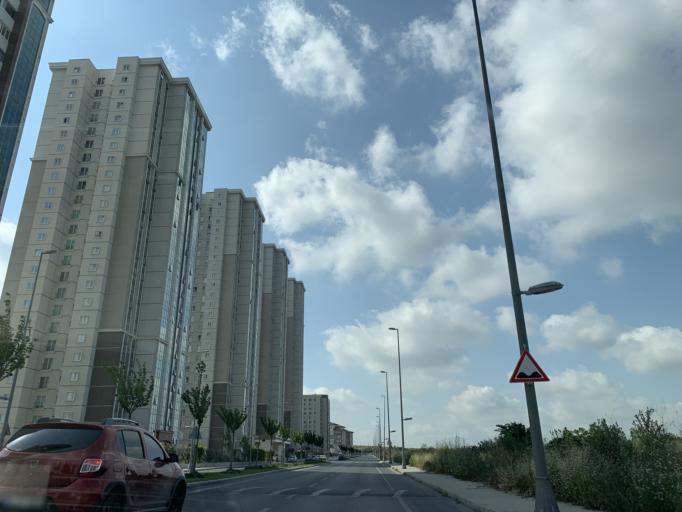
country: TR
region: Istanbul
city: Esenyurt
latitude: 41.0782
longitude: 28.6966
